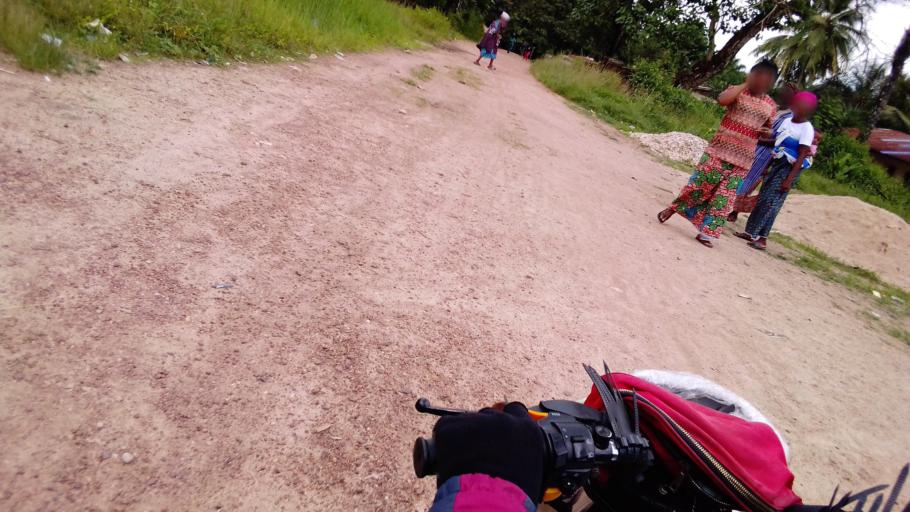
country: SL
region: Eastern Province
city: Koidu
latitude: 8.6751
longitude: -10.9794
